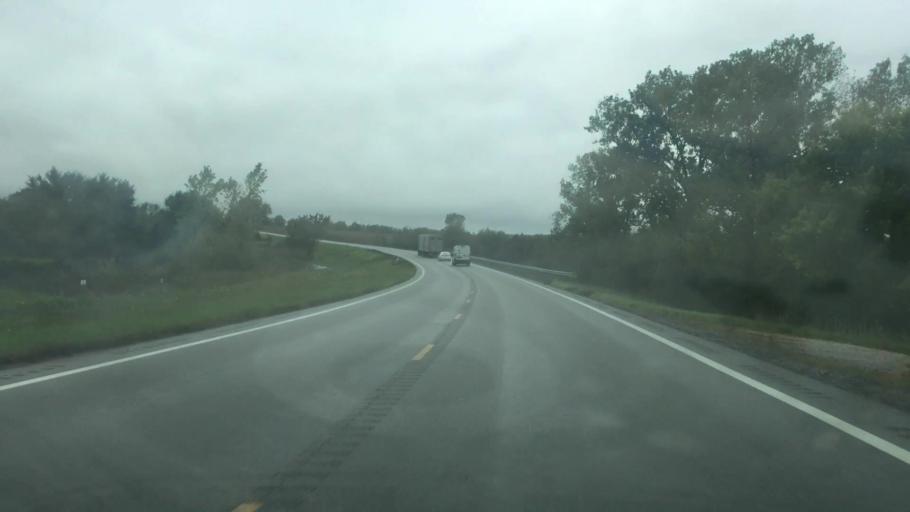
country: US
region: Kansas
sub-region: Anderson County
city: Garnett
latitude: 38.1618
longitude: -95.3072
